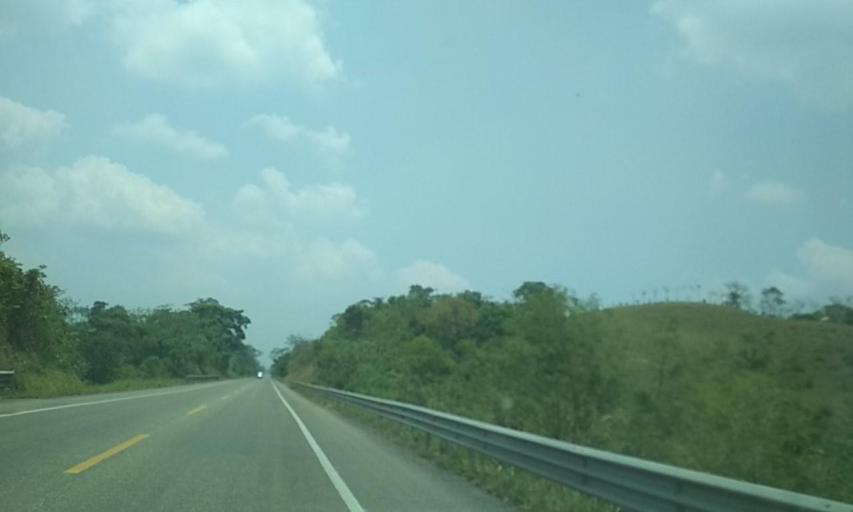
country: MX
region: Tabasco
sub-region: Huimanguillo
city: Francisco Rueda
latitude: 17.6623
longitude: -93.8564
